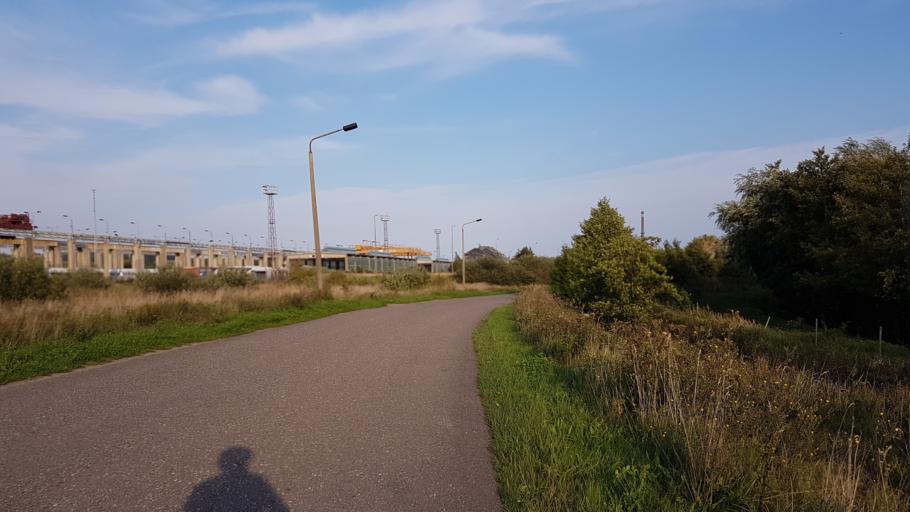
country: DE
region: Mecklenburg-Vorpommern
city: Sagard
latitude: 54.4969
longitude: 13.5495
